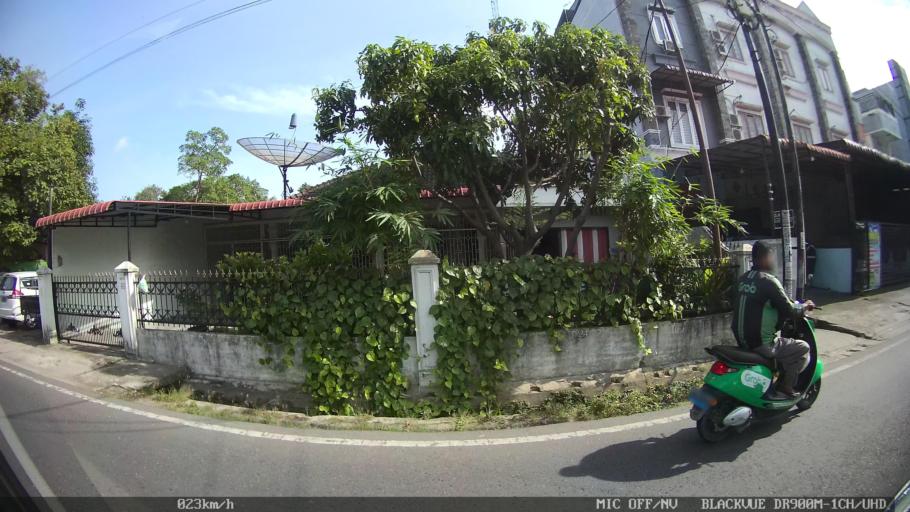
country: ID
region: North Sumatra
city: Medan
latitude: 3.6043
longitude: 98.6528
